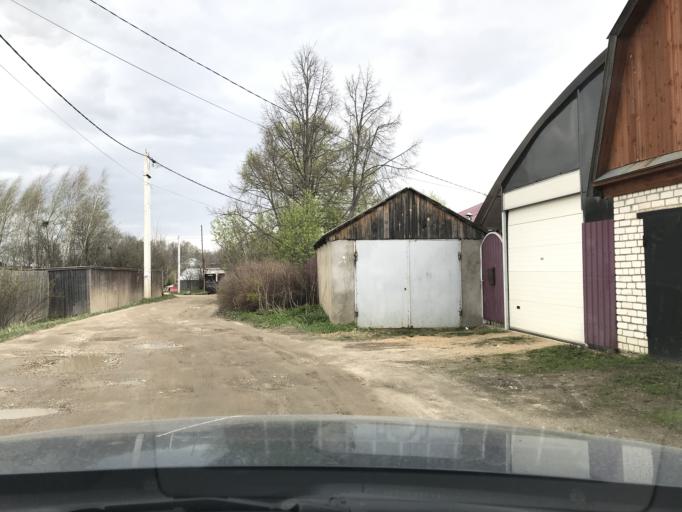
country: RU
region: Vladimir
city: Strunino
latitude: 56.3807
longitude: 38.5943
